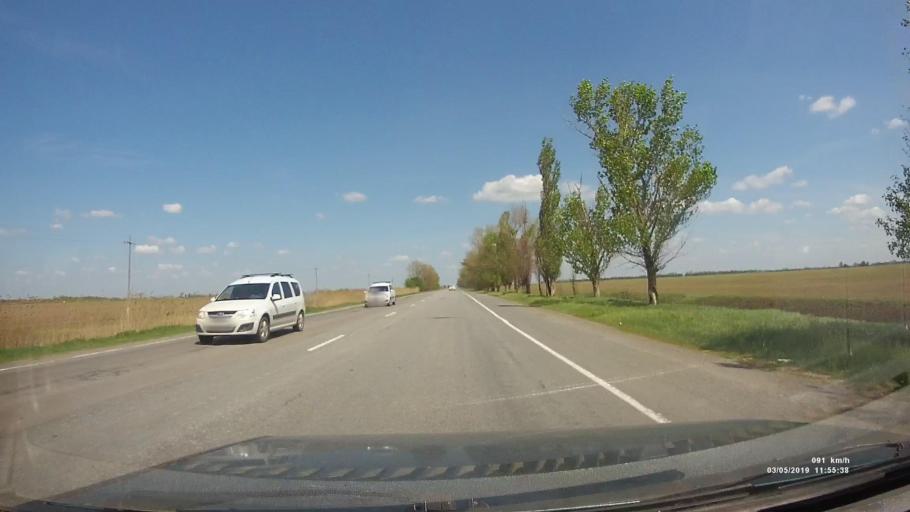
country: RU
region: Rostov
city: Bagayevskaya
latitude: 47.1837
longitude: 40.2930
